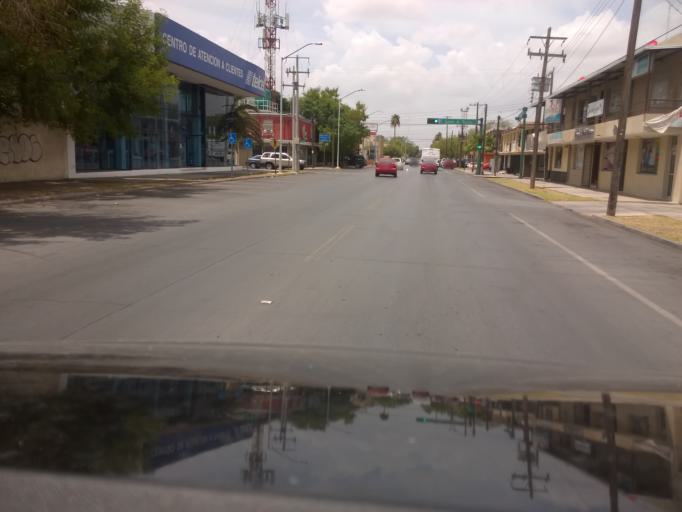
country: MX
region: Tamaulipas
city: Nuevo Laredo
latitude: 27.4867
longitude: -99.5047
